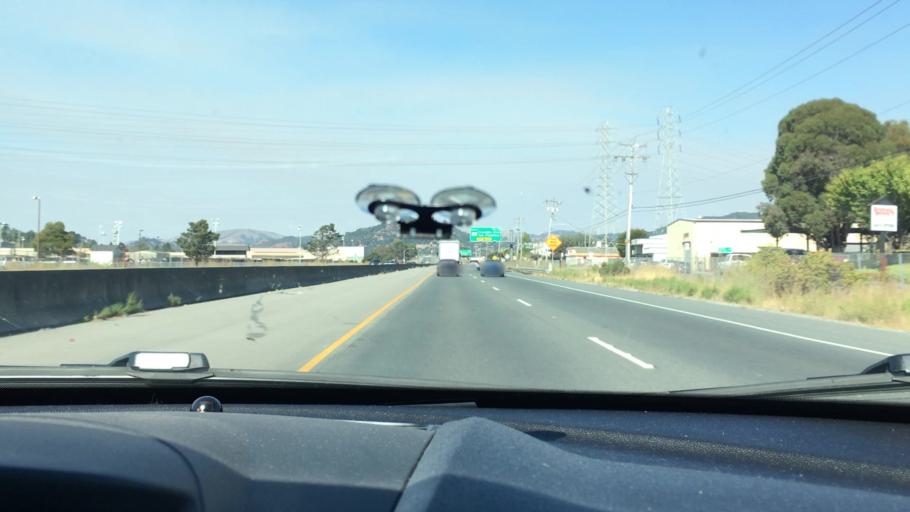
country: US
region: California
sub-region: Marin County
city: San Rafael
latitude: 37.9542
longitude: -122.4993
